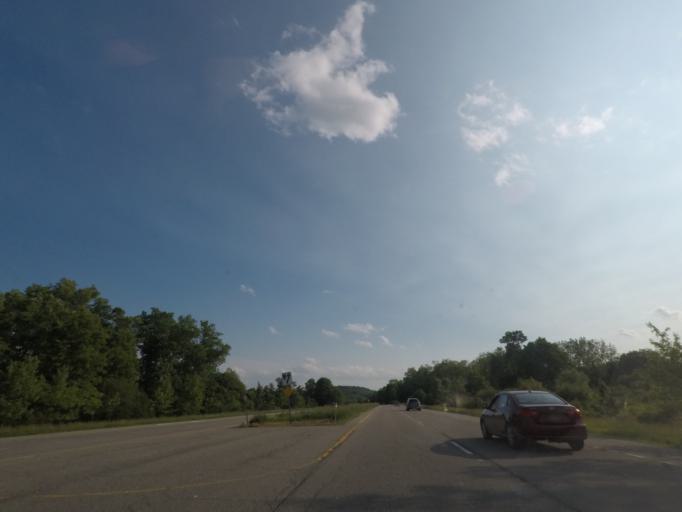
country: US
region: New York
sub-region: Orange County
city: Orange Lake
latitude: 41.5076
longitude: -74.1326
